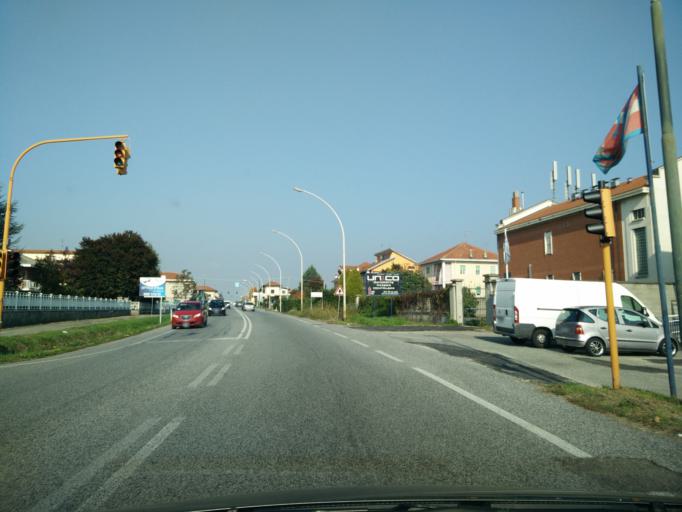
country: IT
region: Piedmont
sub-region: Provincia di Torino
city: Caselle Torinese
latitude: 45.1738
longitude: 7.6513
